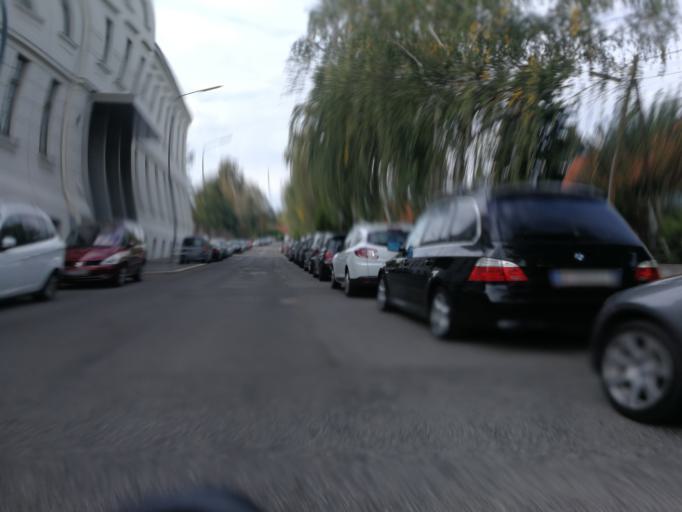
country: AT
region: Vienna
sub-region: Wien Stadt
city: Vienna
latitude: 48.2049
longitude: 16.3019
